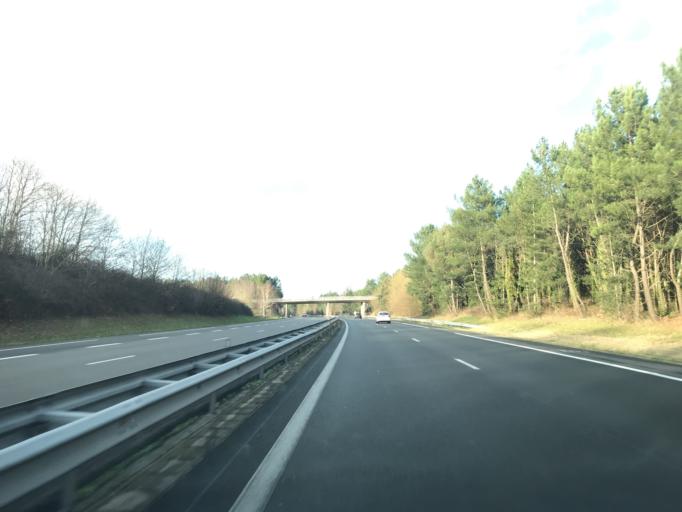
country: FR
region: Pays de la Loire
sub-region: Departement de Maine-et-Loire
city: Seiches-sur-le-Loir
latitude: 47.5623
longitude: -0.3304
